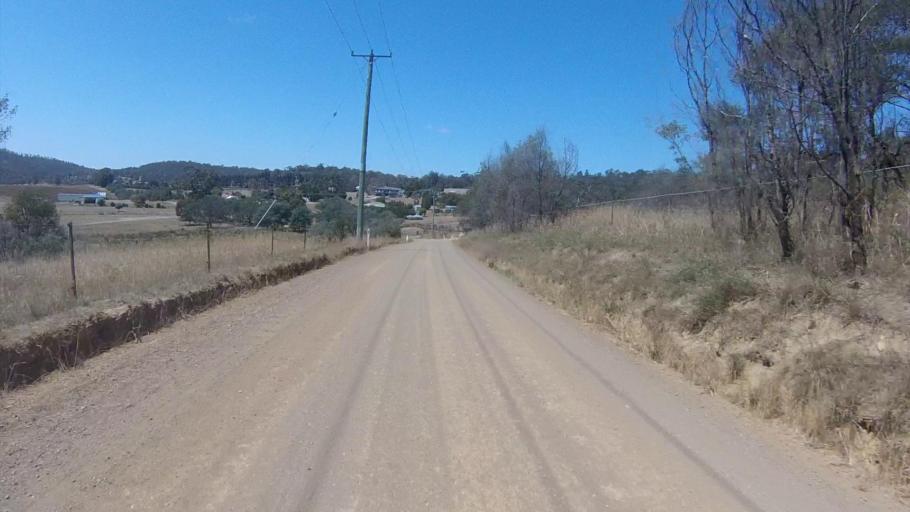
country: AU
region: Tasmania
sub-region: Sorell
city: Sorell
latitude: -42.8251
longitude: 147.6415
